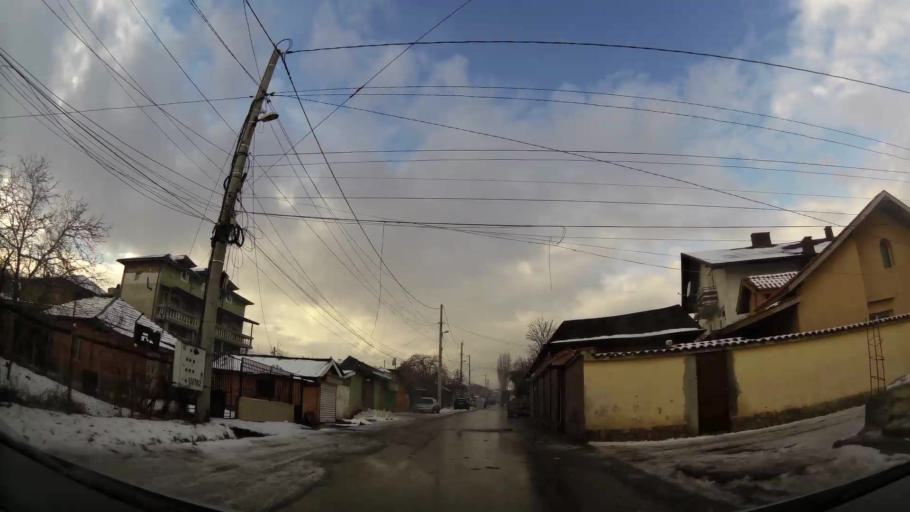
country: BG
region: Sofia-Capital
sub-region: Stolichna Obshtina
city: Sofia
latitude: 42.6954
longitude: 23.2710
